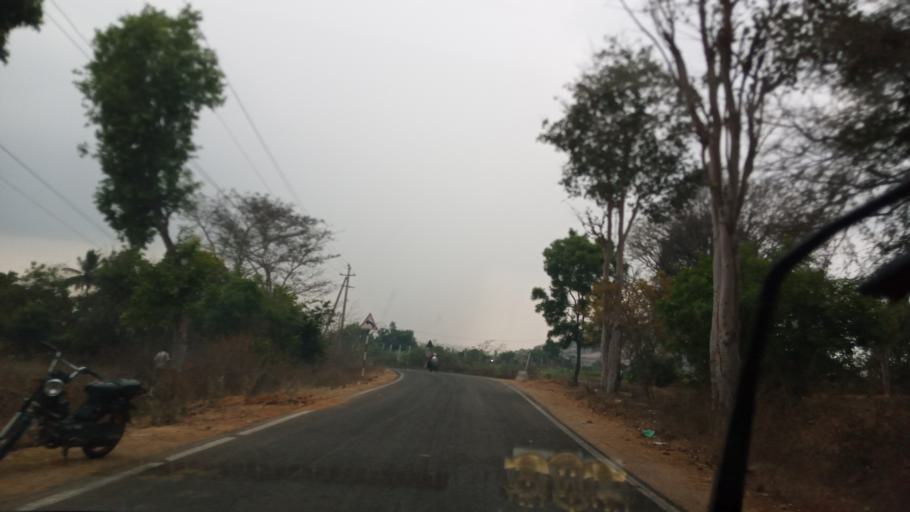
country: IN
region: Karnataka
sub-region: Kolar
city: Mulbagal
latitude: 13.1175
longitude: 78.3372
